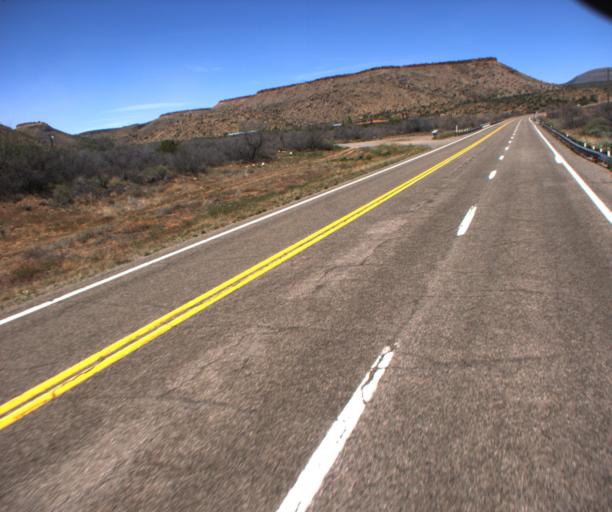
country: US
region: Arizona
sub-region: Mohave County
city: Peach Springs
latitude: 35.4210
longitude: -113.6483
